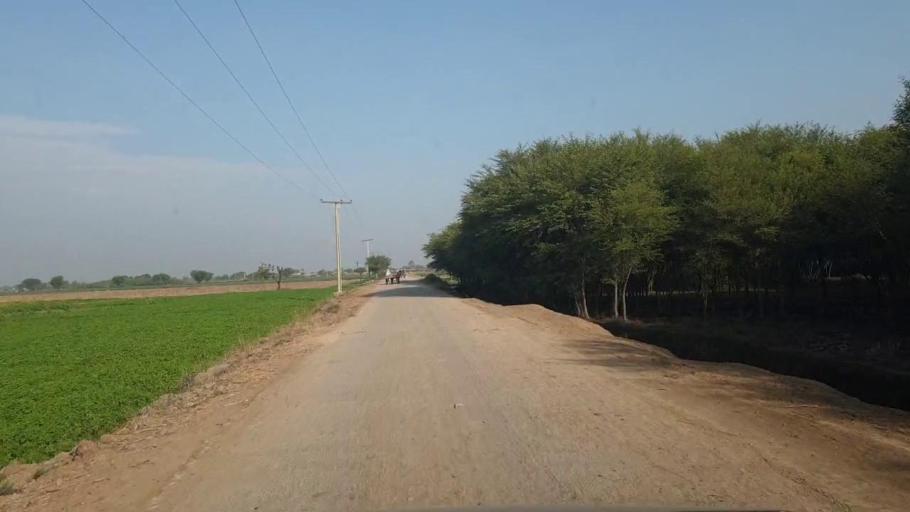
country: PK
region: Sindh
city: Tando Adam
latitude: 25.7399
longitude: 68.6075
